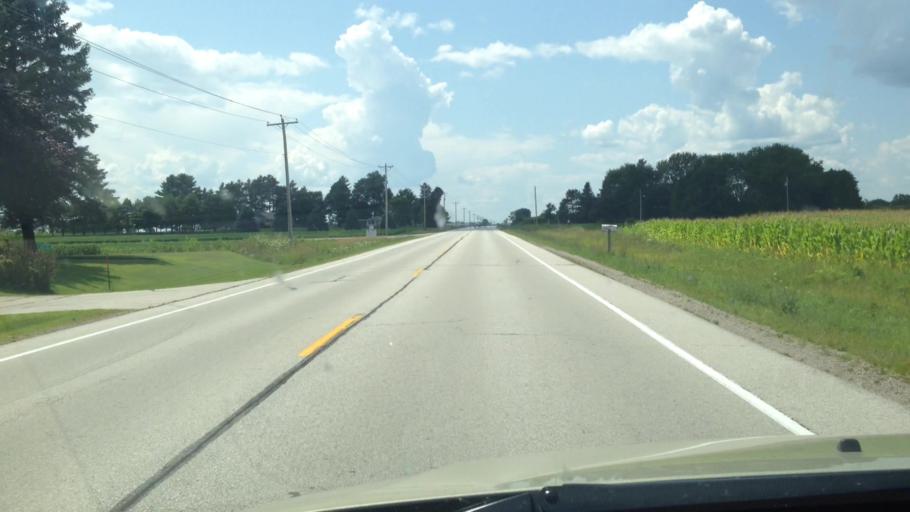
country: US
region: Wisconsin
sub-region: Brown County
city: Pulaski
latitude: 44.6578
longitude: -88.2074
